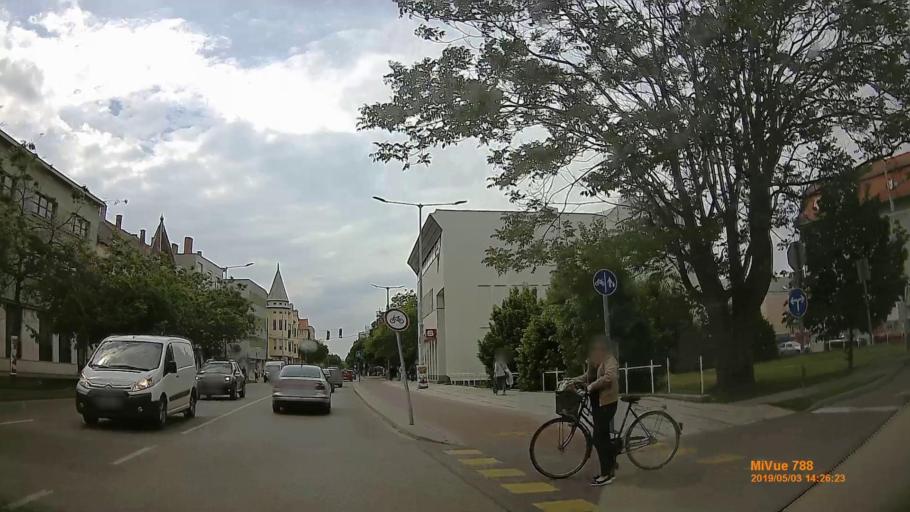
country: HU
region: Jasz-Nagykun-Szolnok
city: Szolnok
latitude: 47.1756
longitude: 20.1919
